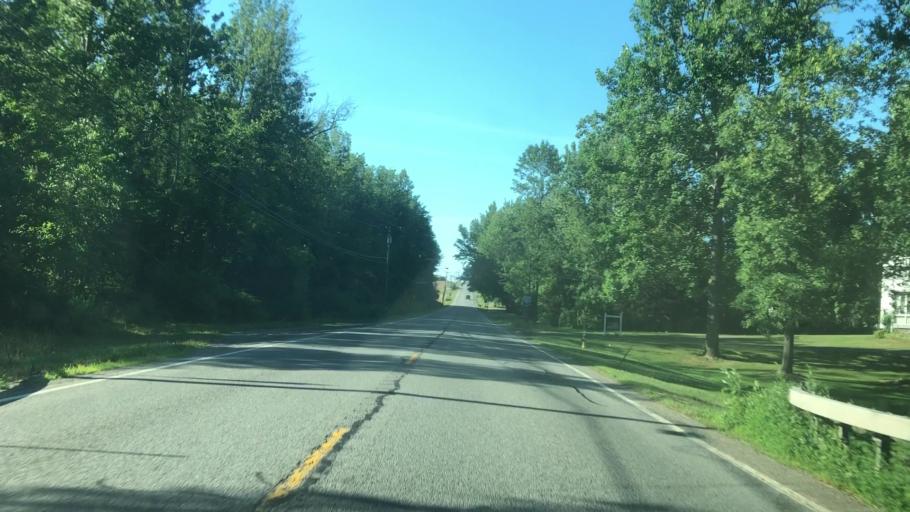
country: US
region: New York
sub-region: Wayne County
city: Macedon
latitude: 43.1300
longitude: -77.2926
